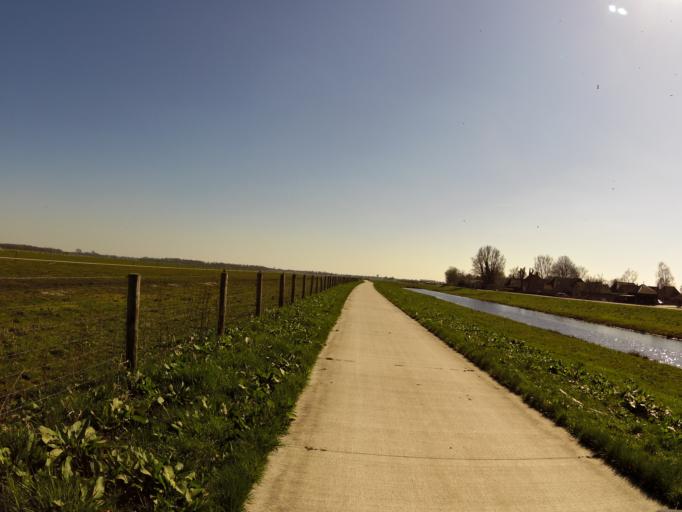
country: NL
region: Overijssel
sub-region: Gemeente Steenwijkerland
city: Blokzijl
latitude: 52.7703
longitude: 5.9887
